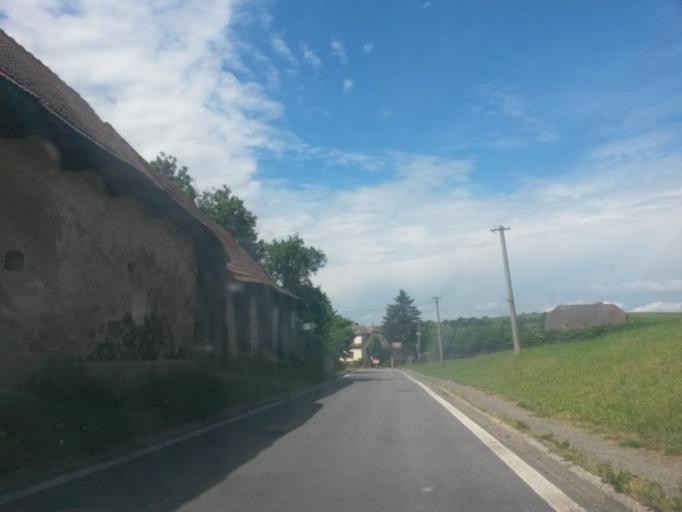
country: CZ
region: Vysocina
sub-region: Okres Zd'ar nad Sazavou
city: Nove Mesto na Morave
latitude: 49.5785
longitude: 16.0985
